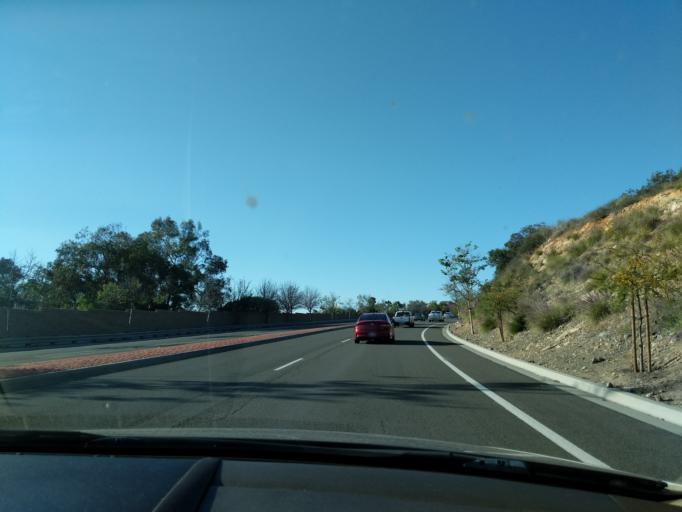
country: US
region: California
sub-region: San Diego County
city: Lake San Marcos
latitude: 33.1139
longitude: -117.2267
